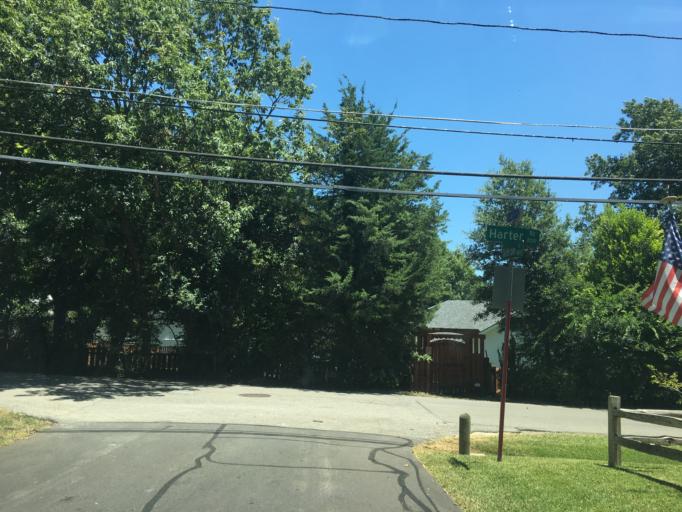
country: US
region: Texas
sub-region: Dallas County
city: Highland Park
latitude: 32.8457
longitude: -96.7098
